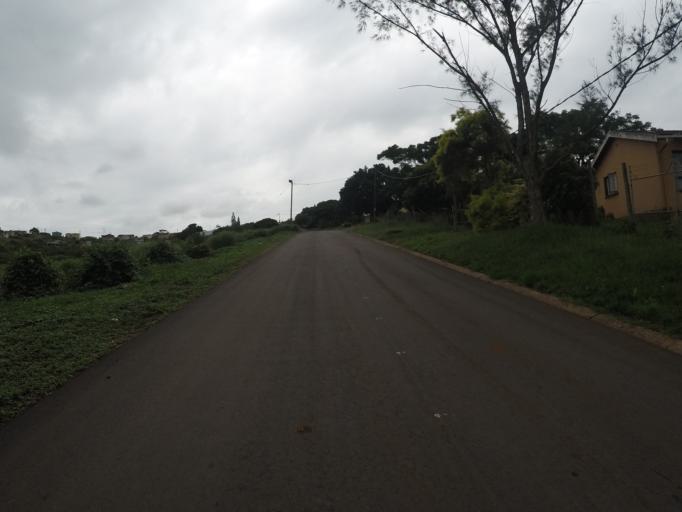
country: ZA
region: KwaZulu-Natal
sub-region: uThungulu District Municipality
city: Empangeni
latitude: -28.7721
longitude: 31.8610
